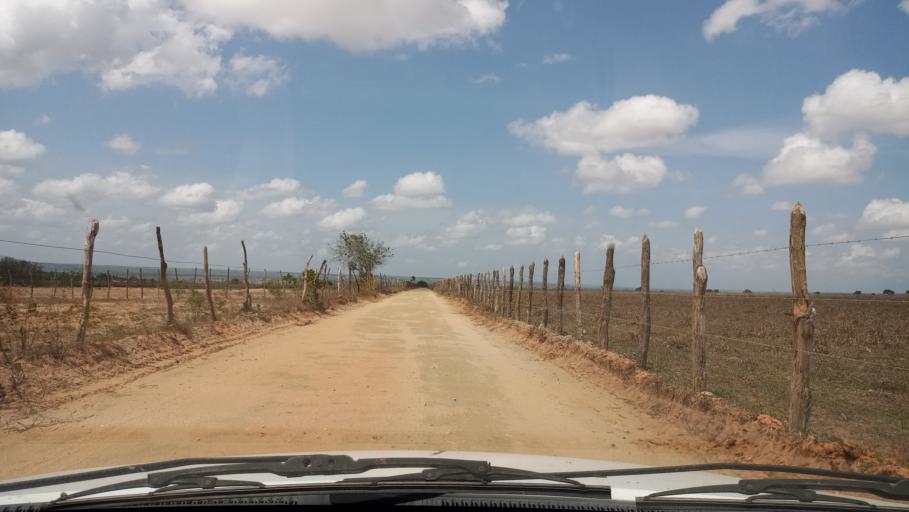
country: BR
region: Rio Grande do Norte
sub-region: Montanhas
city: Montanhas
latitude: -6.3516
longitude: -35.3333
